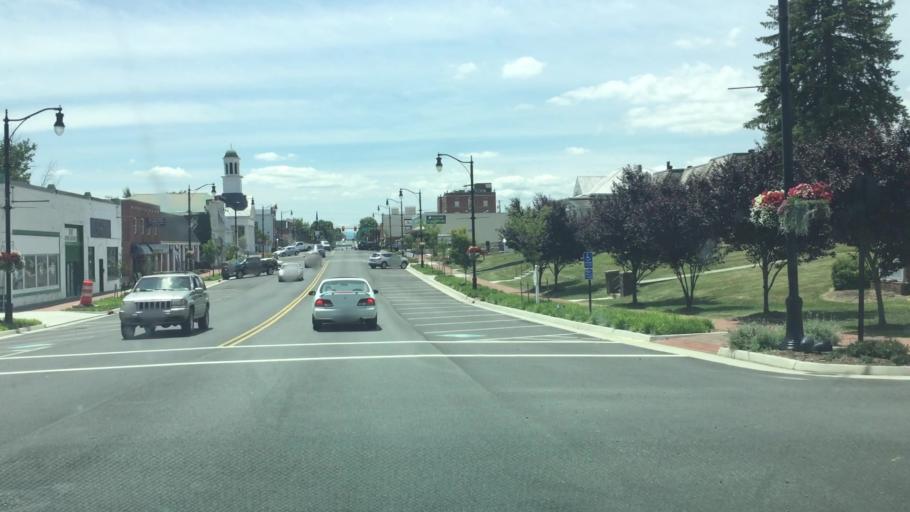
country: US
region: Virginia
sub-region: Wythe County
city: Wytheville
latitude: 36.9519
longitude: -81.0808
